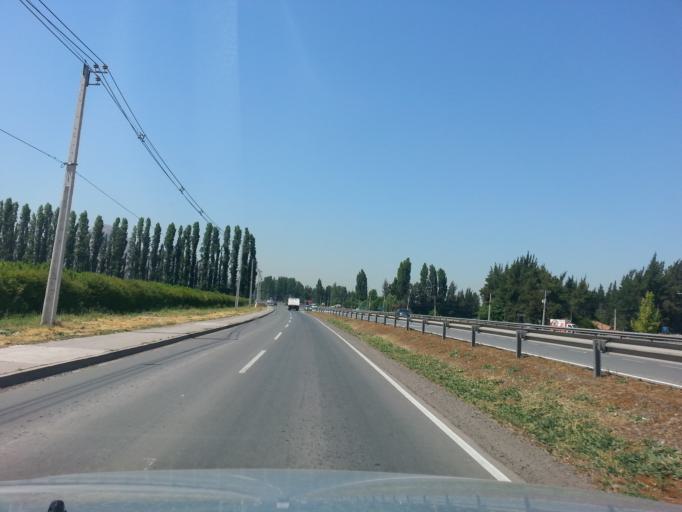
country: CL
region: Santiago Metropolitan
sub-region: Provincia de Chacabuco
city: Chicureo Abajo
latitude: -33.2780
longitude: -70.7024
